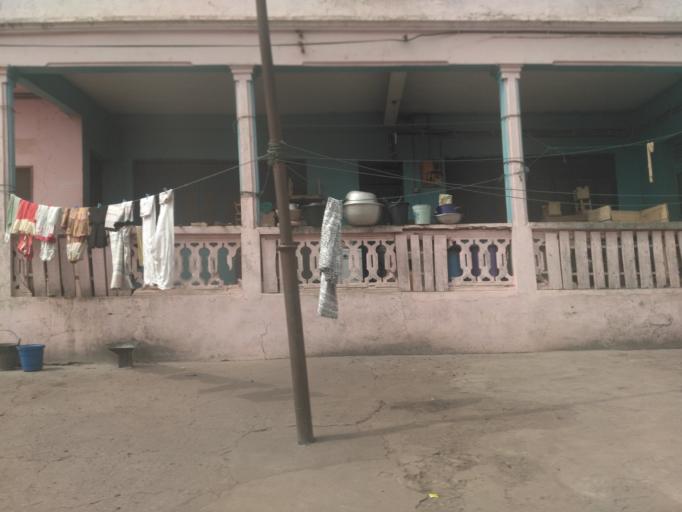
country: GH
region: Ashanti
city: Tafo
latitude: 6.7111
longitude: -1.6126
